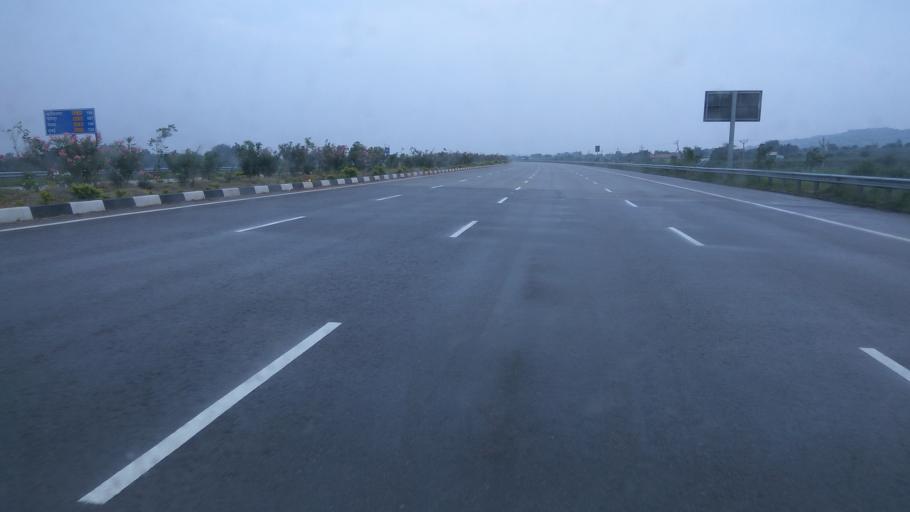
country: IN
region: Telangana
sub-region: Rangareddi
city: Ghatkesar
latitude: 17.4699
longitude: 78.6705
